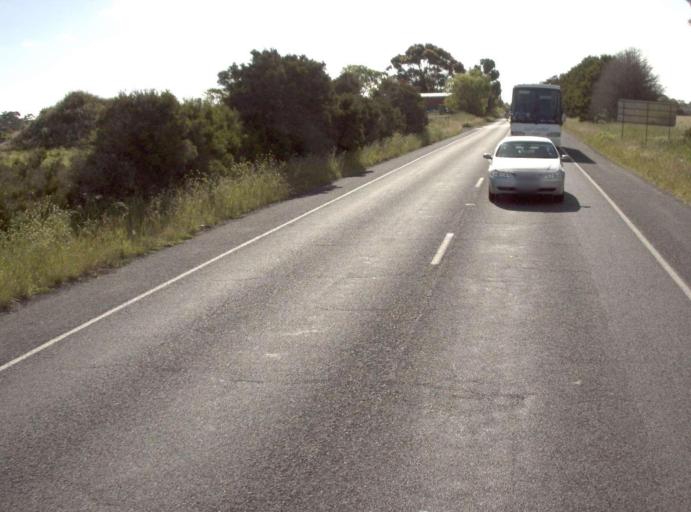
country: AU
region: Victoria
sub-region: Bass Coast
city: North Wonthaggi
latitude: -38.6087
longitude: 145.6196
